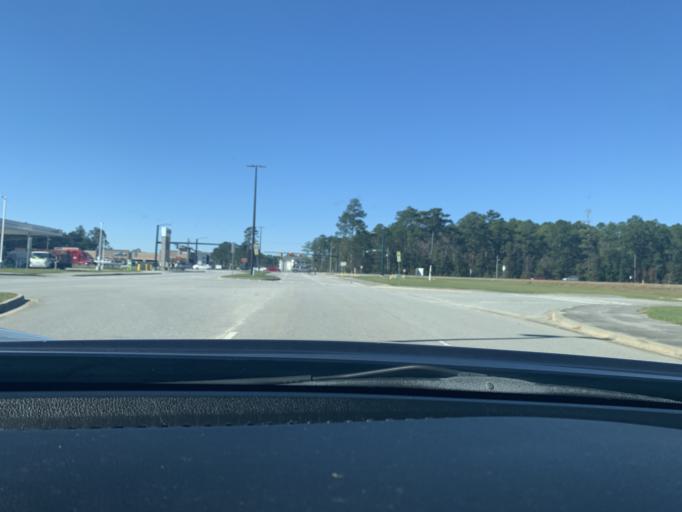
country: US
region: Georgia
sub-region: Chatham County
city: Pooler
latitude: 32.0878
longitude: -81.2758
